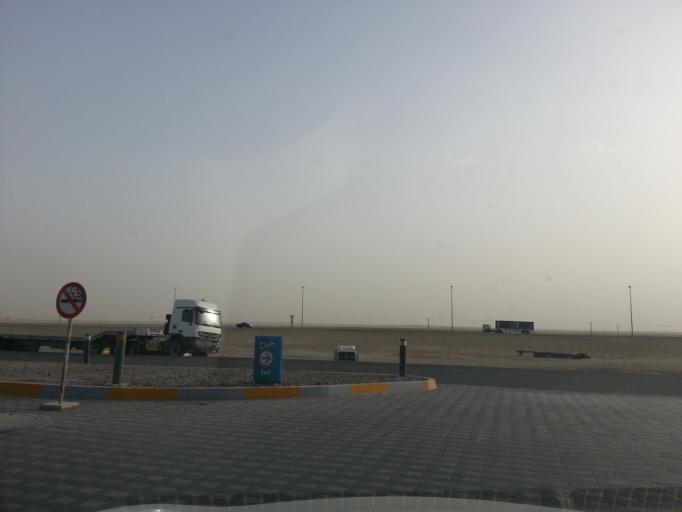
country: AE
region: Dubai
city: Dubai
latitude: 24.8061
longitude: 55.0699
